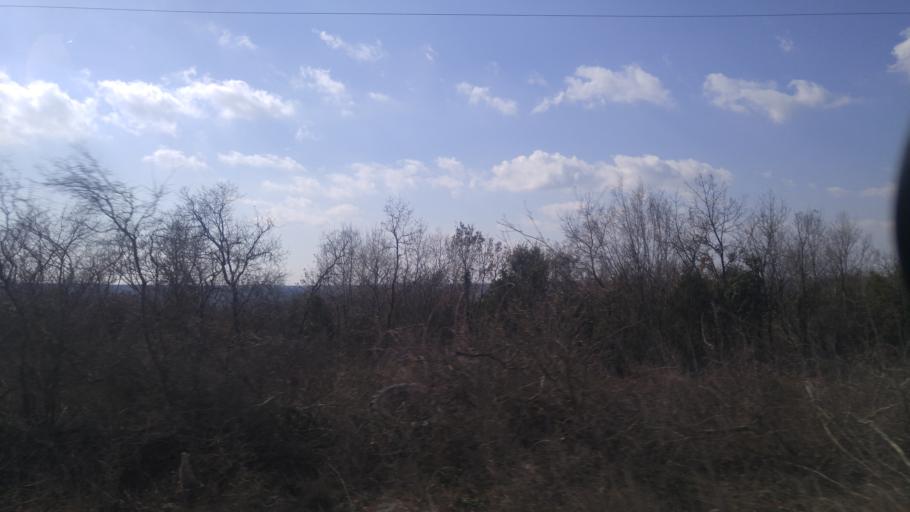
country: TR
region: Istanbul
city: Buyukcavuslu
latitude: 41.1836
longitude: 28.0864
